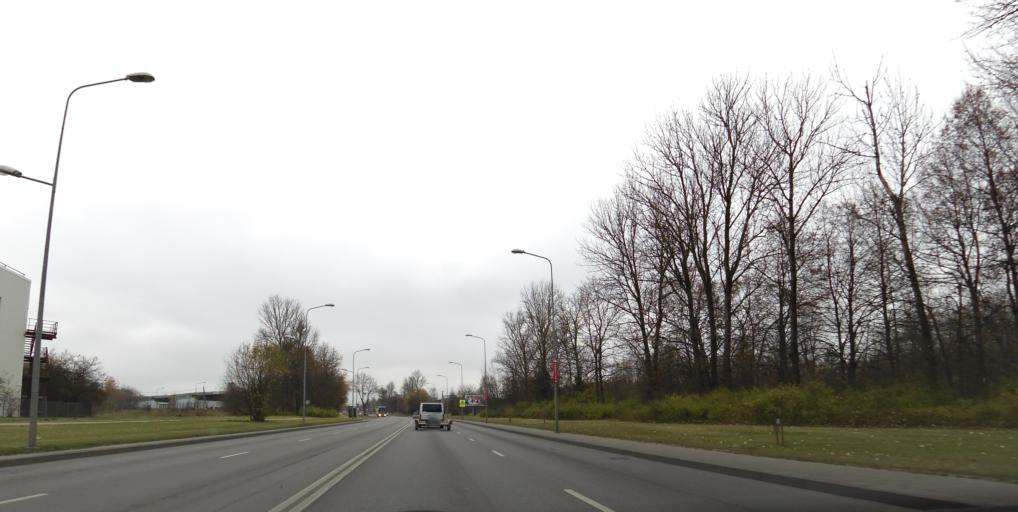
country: LT
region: Vilnius County
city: Naujamiestis
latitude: 54.6507
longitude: 25.2695
